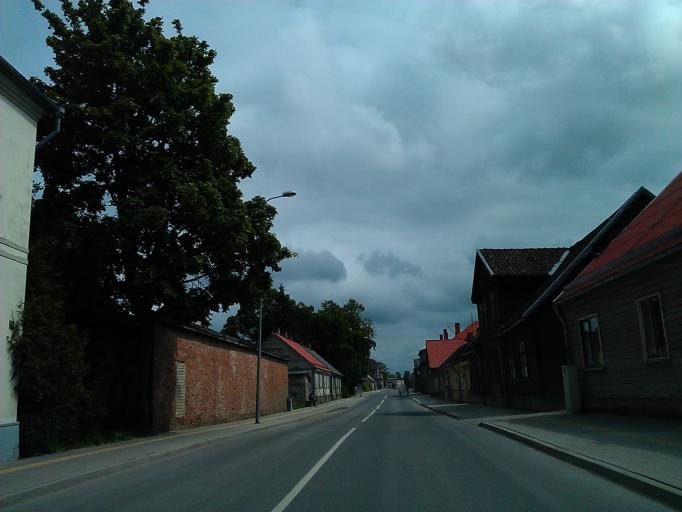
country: LV
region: Aizpute
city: Aizpute
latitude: 56.7179
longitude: 21.6075
